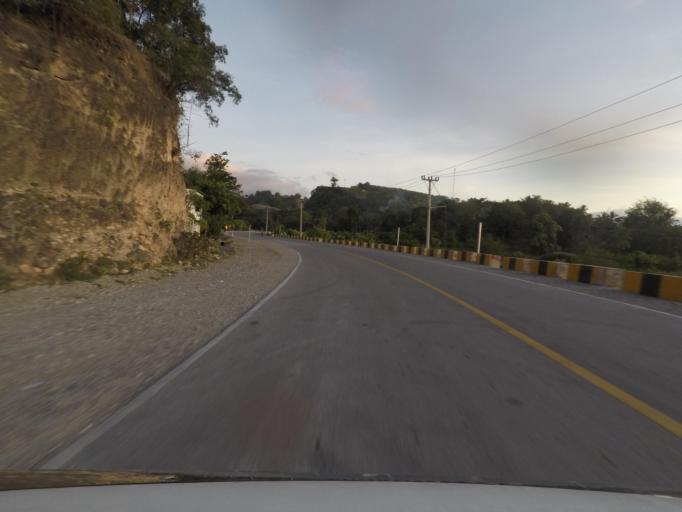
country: TL
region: Baucau
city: Baucau
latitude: -8.4698
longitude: 126.6028
